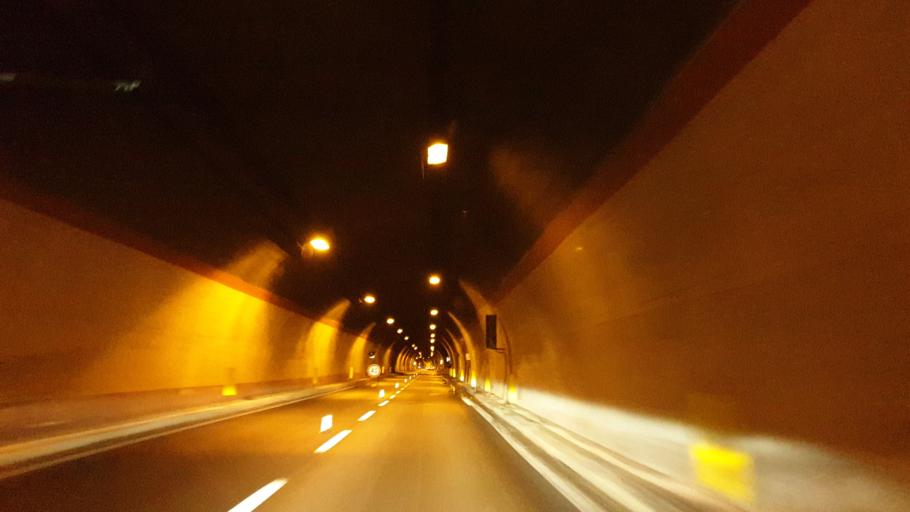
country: IT
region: Emilia-Romagna
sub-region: Forli-Cesena
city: Sarsina
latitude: 43.8982
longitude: 12.0953
